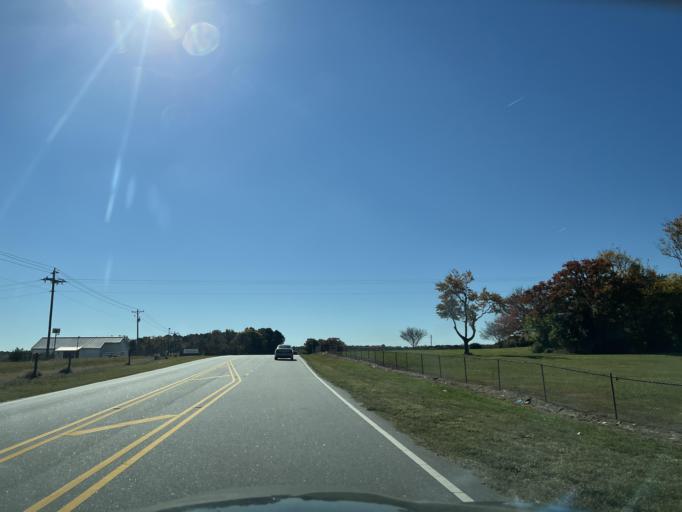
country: US
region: North Carolina
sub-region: Wake County
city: West Raleigh
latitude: 35.7257
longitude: -78.6836
